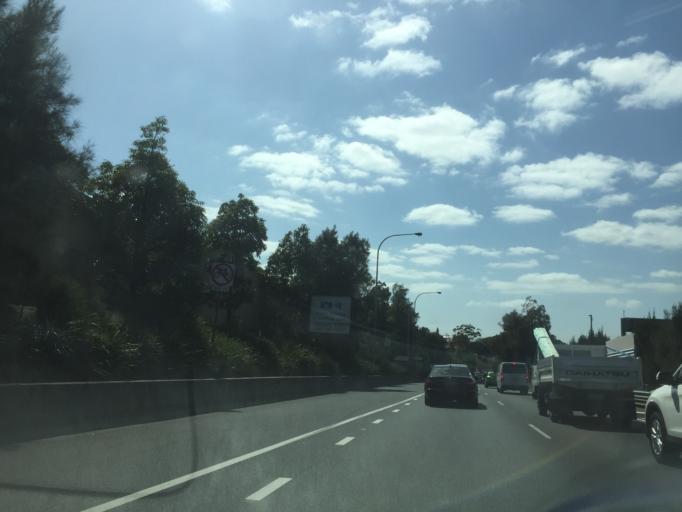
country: AU
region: New South Wales
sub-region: Rockdale
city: Bexley North
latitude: -33.9363
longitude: 151.1075
